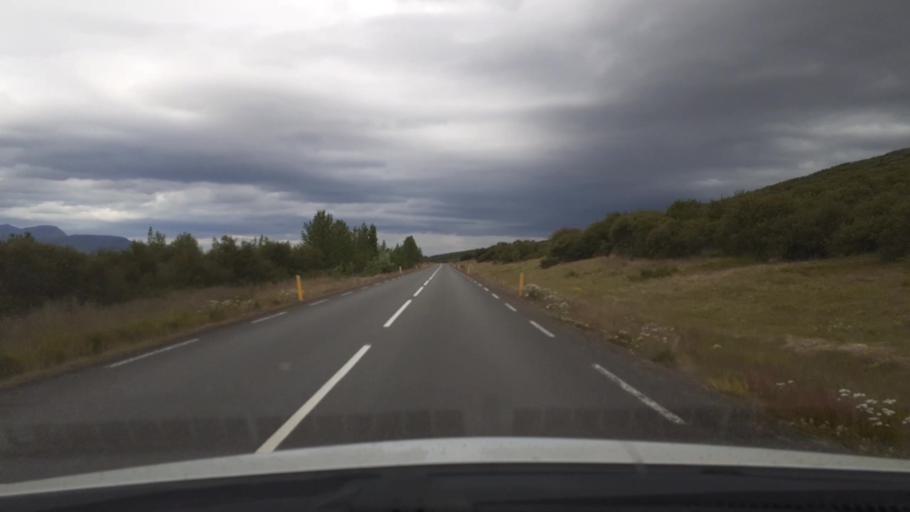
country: IS
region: West
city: Borgarnes
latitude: 64.5414
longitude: -21.5476
